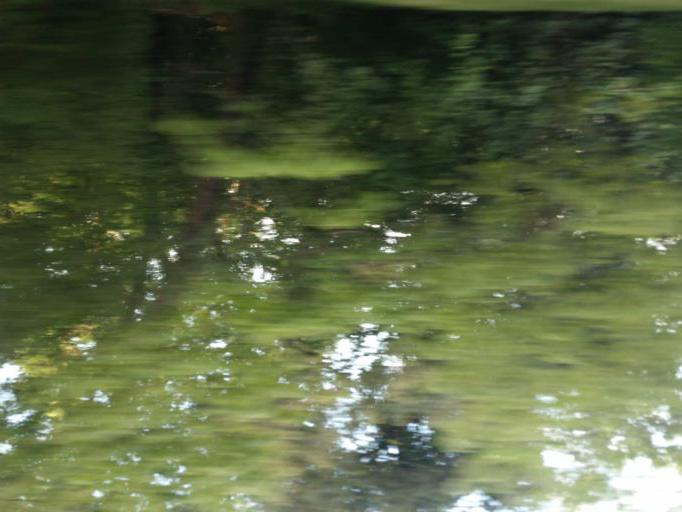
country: US
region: Tennessee
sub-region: Knox County
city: Knoxville
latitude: 36.0441
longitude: -83.9401
